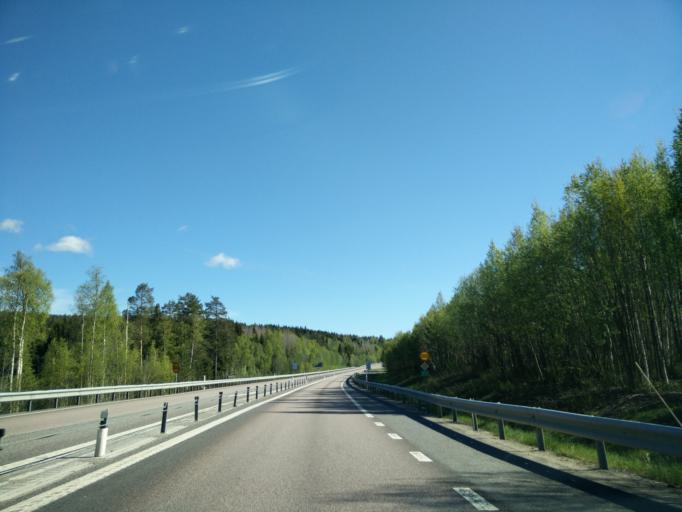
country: SE
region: Vaesternorrland
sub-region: Kramfors Kommun
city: Nordingra
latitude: 62.9504
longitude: 18.0948
